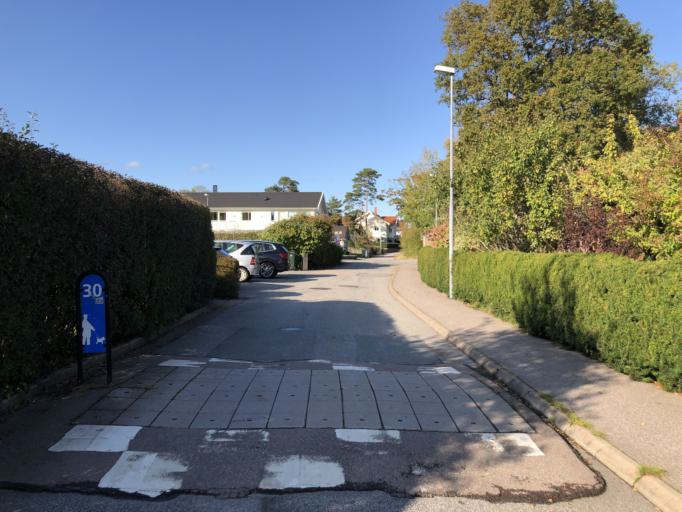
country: SE
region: Vaestra Goetaland
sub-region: Goteborg
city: Billdal
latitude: 57.6224
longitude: 11.8846
